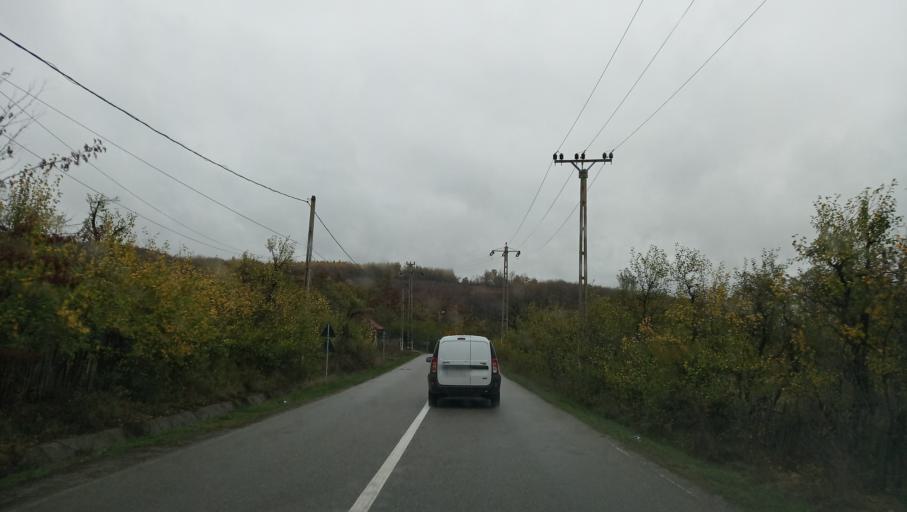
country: RO
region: Gorj
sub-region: Comuna Crasna
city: Crasna
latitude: 45.1790
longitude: 23.5174
